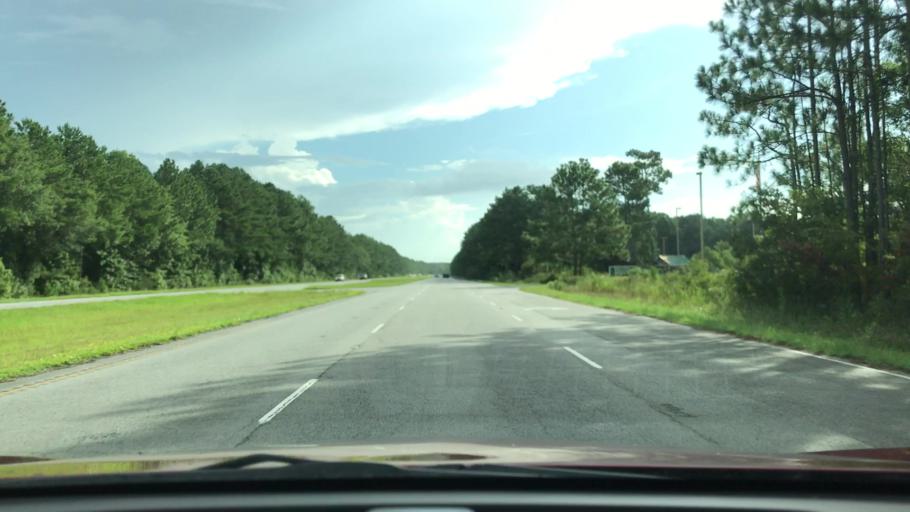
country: US
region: South Carolina
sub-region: Charleston County
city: Awendaw
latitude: 32.9747
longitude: -79.6700
